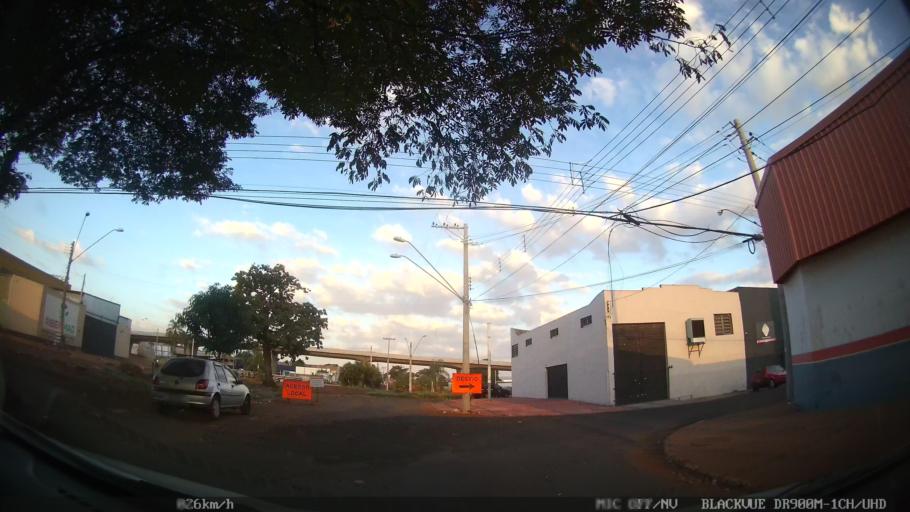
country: BR
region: Sao Paulo
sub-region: Ribeirao Preto
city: Ribeirao Preto
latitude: -21.1463
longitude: -47.7910
